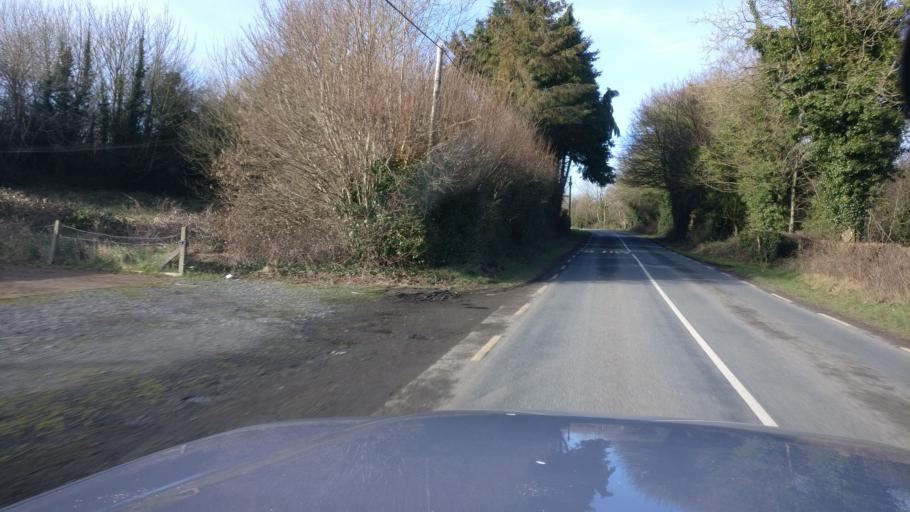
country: IE
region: Leinster
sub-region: Laois
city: Stradbally
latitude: 52.9669
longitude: -7.2067
